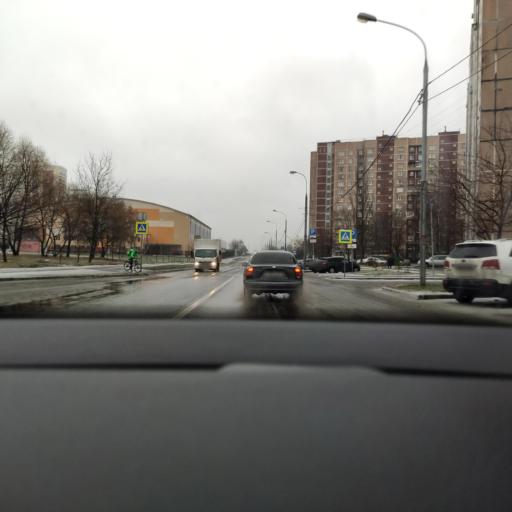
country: RU
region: Moskovskaya
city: Reutov
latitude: 55.7454
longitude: 37.8711
